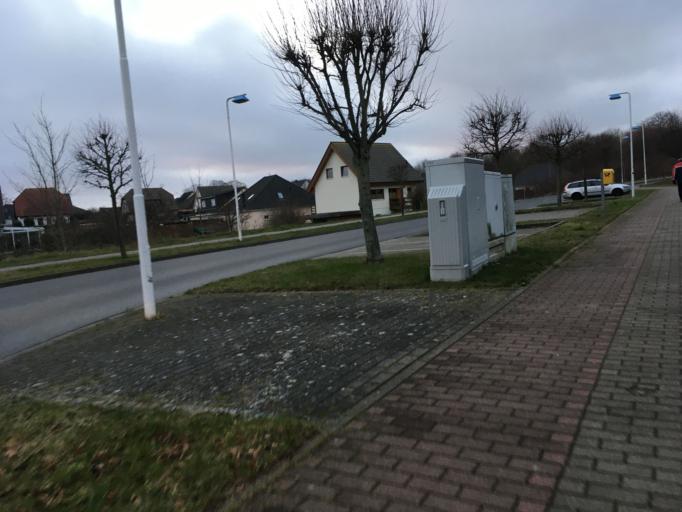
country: DE
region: Mecklenburg-Vorpommern
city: Sassnitz
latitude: 54.5121
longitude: 13.6064
